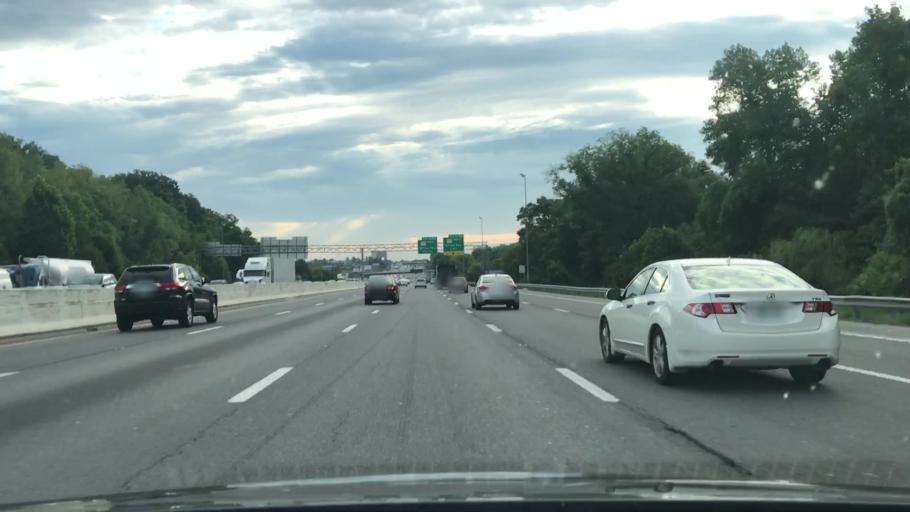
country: US
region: Tennessee
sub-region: Davidson County
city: Nashville
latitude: 36.1404
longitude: -86.7197
